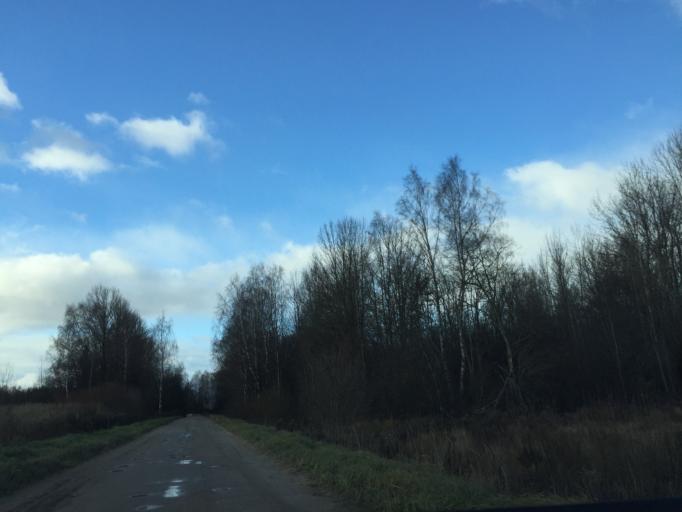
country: LV
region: Valmieras Rajons
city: Valmiera
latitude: 57.5375
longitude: 25.3876
